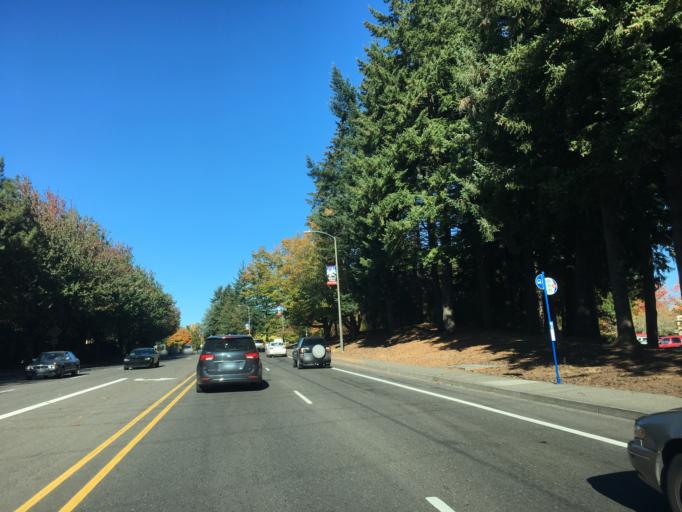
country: US
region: Oregon
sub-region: Multnomah County
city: Wood Village
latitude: 45.5130
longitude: -122.3996
